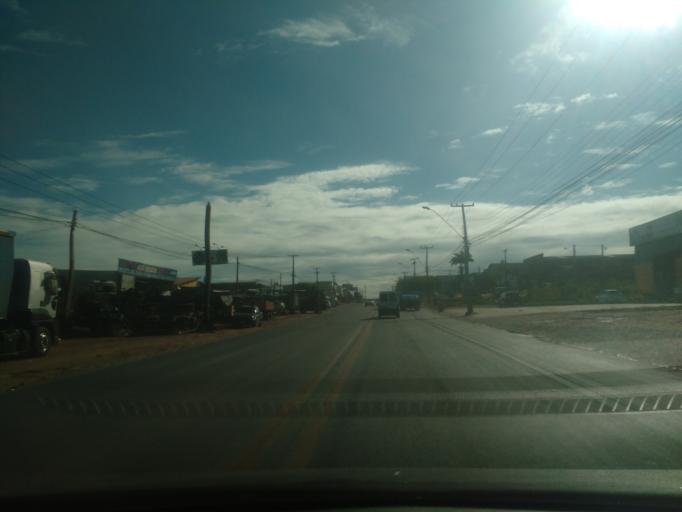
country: BR
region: Alagoas
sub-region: Satuba
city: Satuba
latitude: -9.5625
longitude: -35.7701
